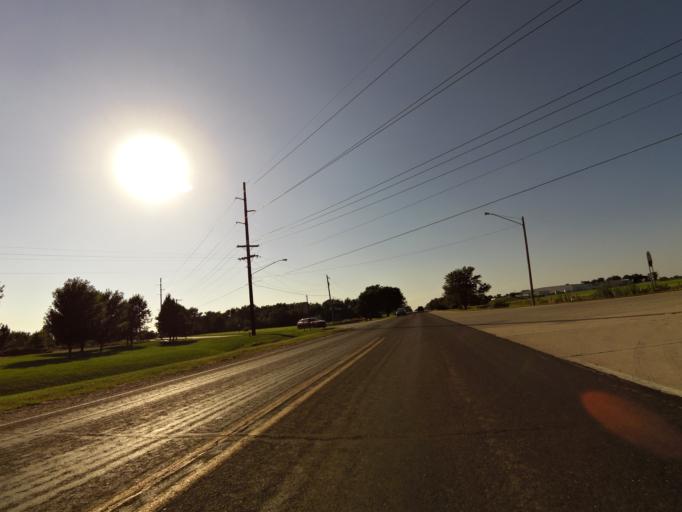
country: US
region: Kansas
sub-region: Harvey County
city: Hesston
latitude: 38.1299
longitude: -97.4203
